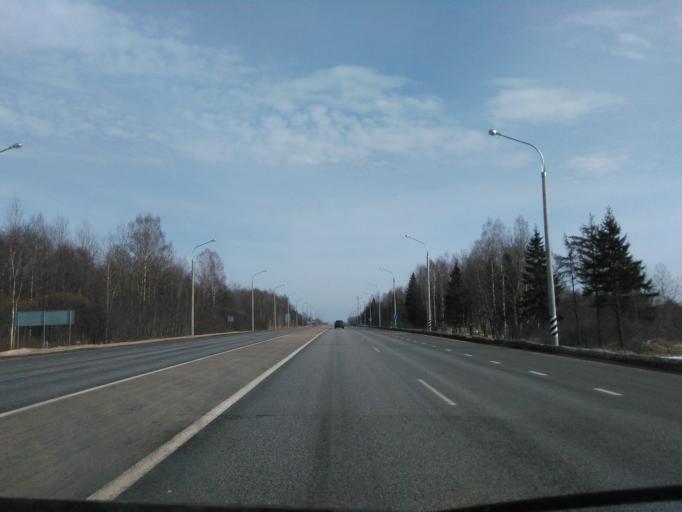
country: RU
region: Smolensk
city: Rudnya
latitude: 54.6905
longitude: 30.9711
